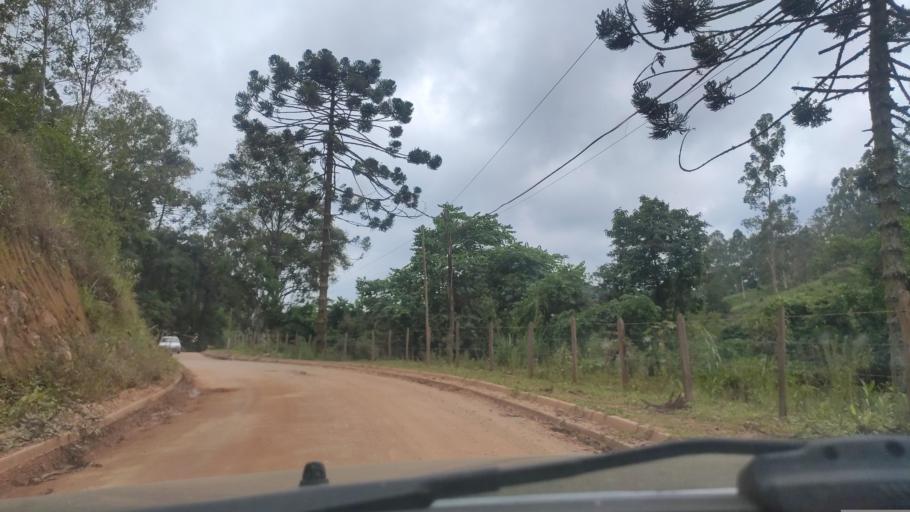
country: BR
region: Minas Gerais
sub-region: Paraisopolis
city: Paraisopolis
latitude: -22.6662
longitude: -45.8532
